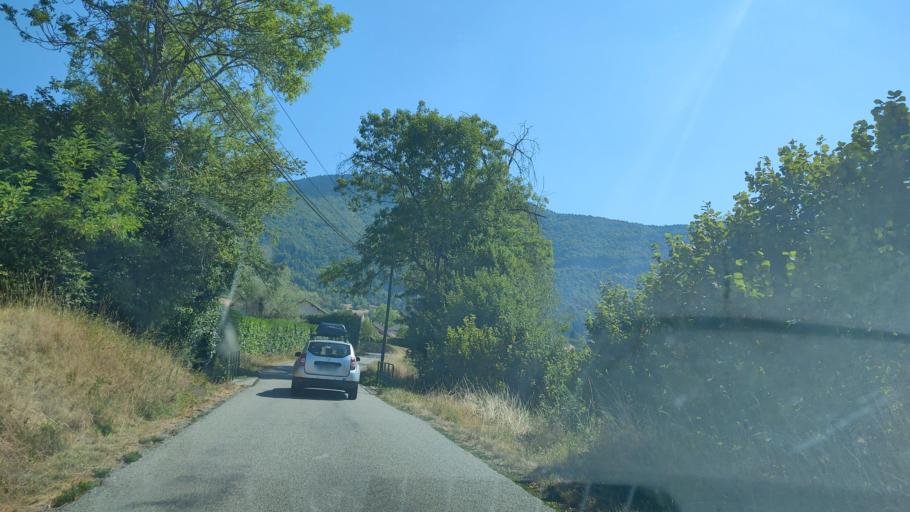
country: FR
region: Rhone-Alpes
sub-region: Departement de la Savoie
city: Novalaise
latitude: 45.5981
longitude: 5.7786
